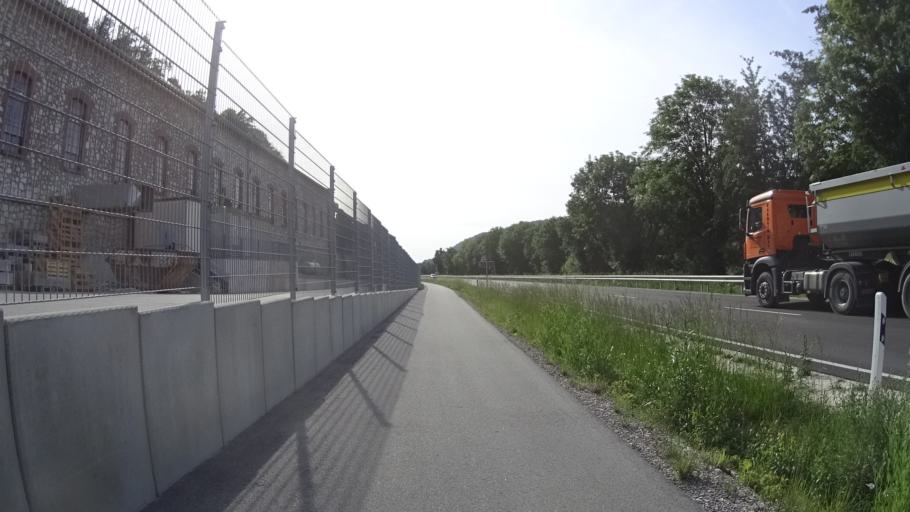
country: DE
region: Bavaria
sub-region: Lower Bavaria
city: Ihrlerstein
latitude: 48.9265
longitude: 11.8306
